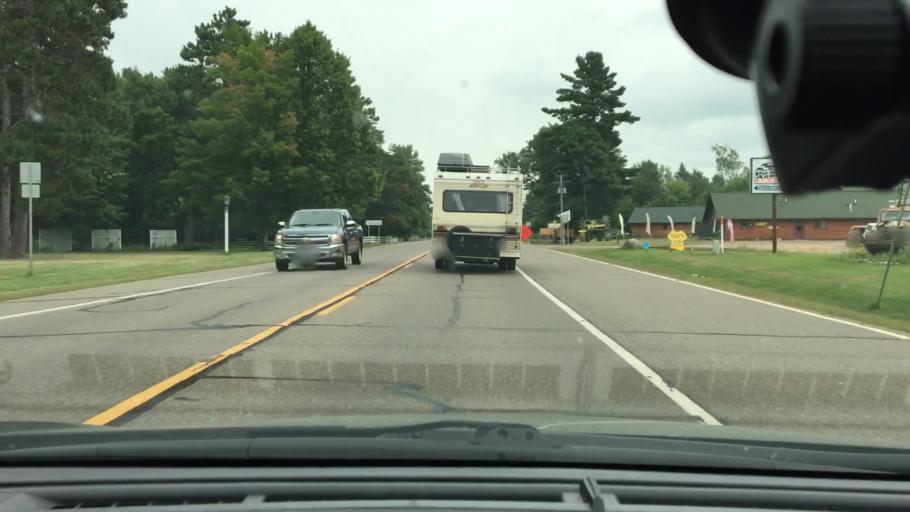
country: US
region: Minnesota
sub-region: Crow Wing County
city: Crosby
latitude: 46.4860
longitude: -93.9349
